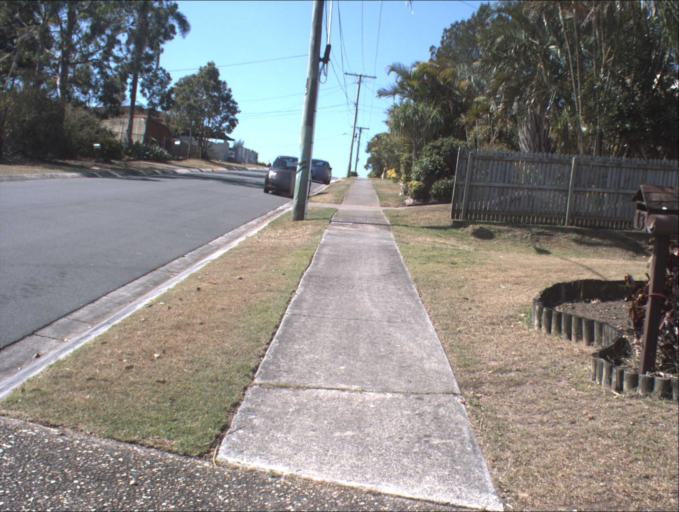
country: AU
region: Queensland
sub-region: Logan
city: Slacks Creek
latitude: -27.6594
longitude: 153.1752
